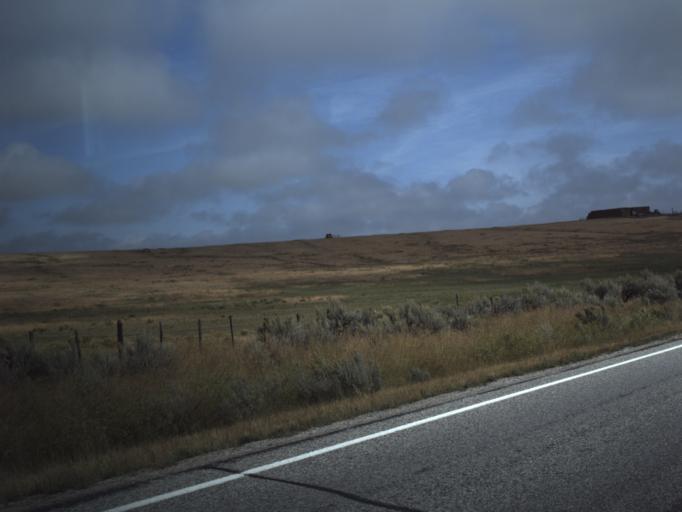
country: US
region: Utah
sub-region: Rich County
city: Randolph
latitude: 41.6978
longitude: -111.1700
